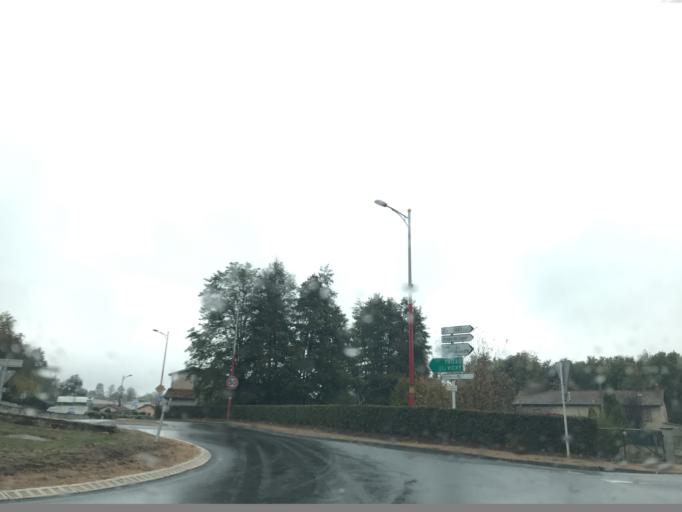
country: FR
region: Auvergne
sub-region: Departement du Puy-de-Dome
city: Courpiere
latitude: 45.7633
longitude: 3.5406
